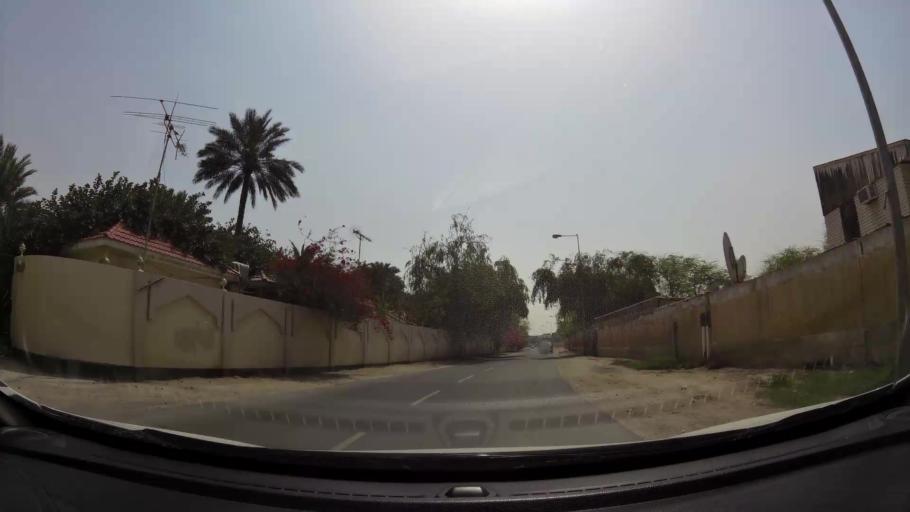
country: BH
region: Manama
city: Jidd Hafs
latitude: 26.2210
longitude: 50.4848
